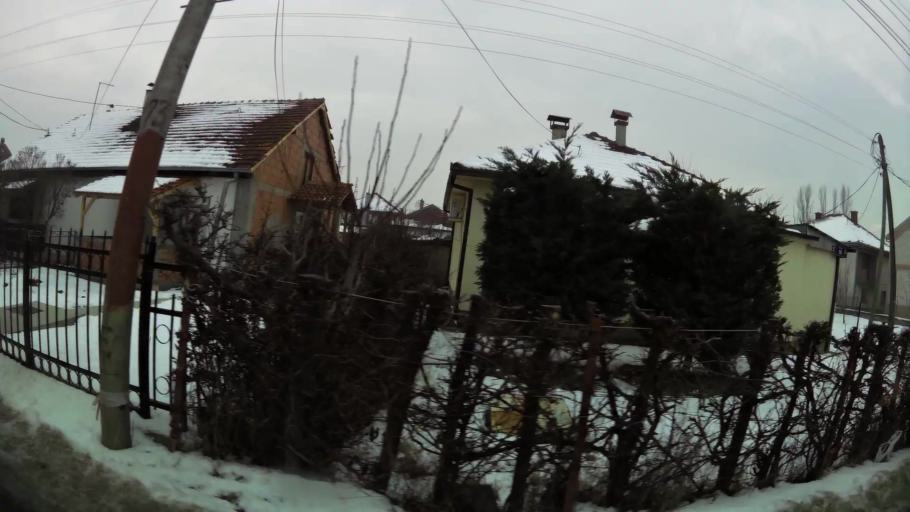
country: MK
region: Saraj
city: Saraj
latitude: 42.0457
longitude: 21.3579
